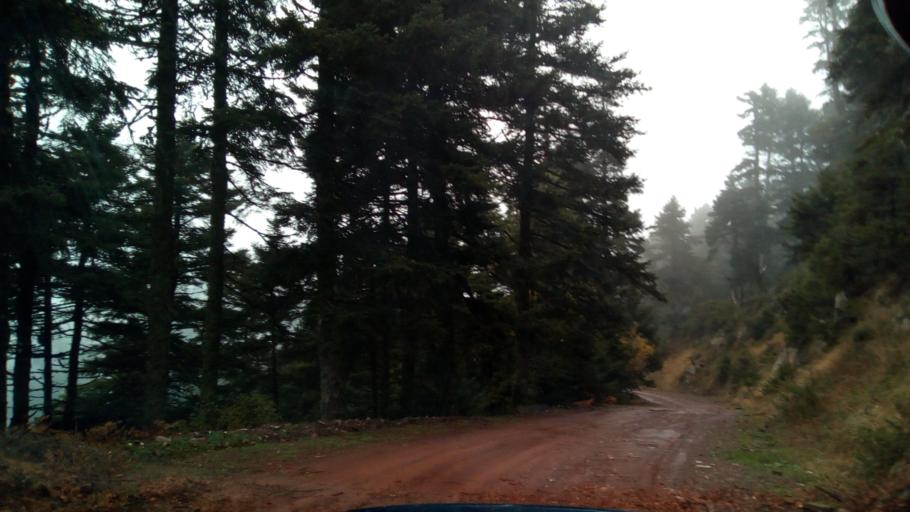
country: GR
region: West Greece
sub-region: Nomos Aitolias kai Akarnanias
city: Nafpaktos
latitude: 38.5420
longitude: 21.8683
